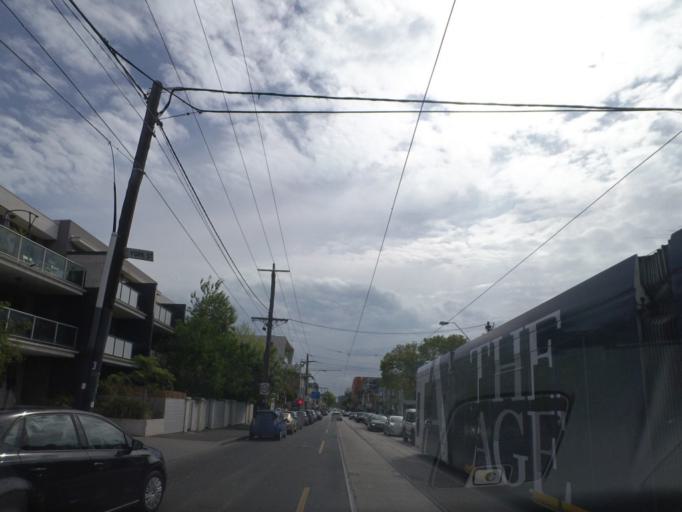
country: AU
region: Victoria
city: Windsor
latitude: -37.8526
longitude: 144.9980
